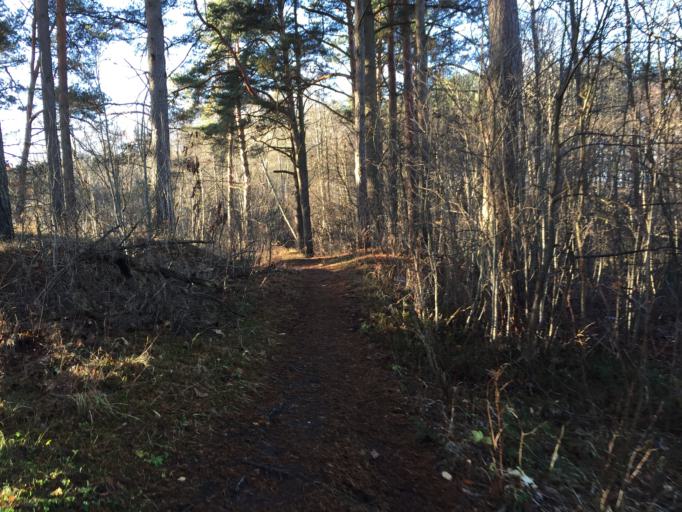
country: LV
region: Valmieras Rajons
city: Valmiera
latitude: 57.5280
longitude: 25.4042
